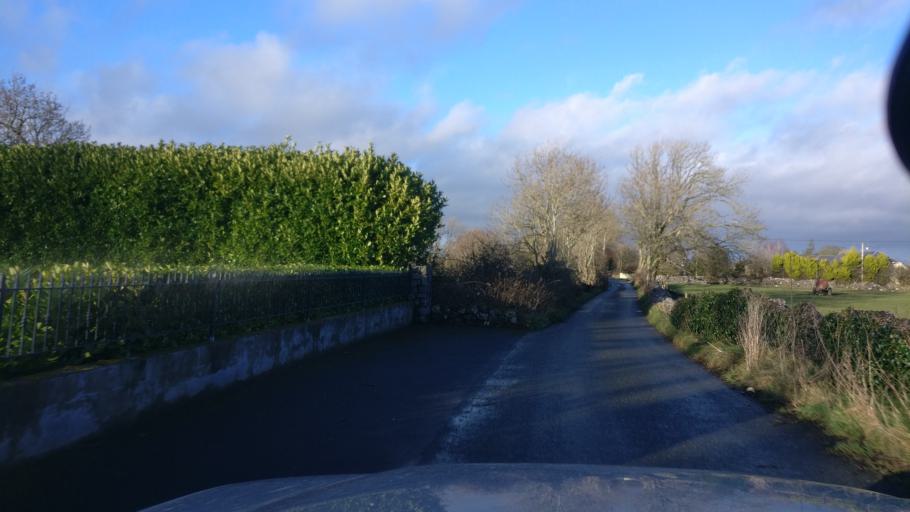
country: IE
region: Connaught
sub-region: County Galway
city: Loughrea
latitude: 53.2347
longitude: -8.5766
